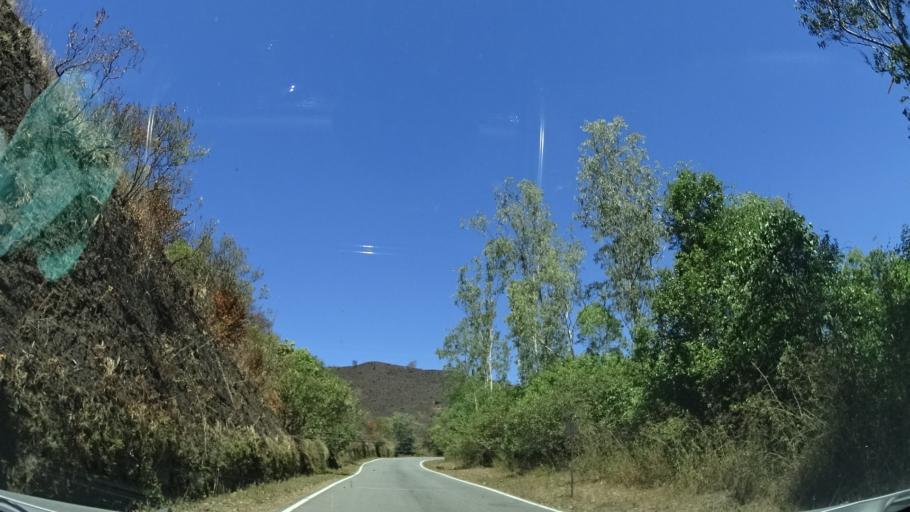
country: IN
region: Karnataka
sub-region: Chikmagalur
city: Sringeri
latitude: 13.2147
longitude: 75.2316
